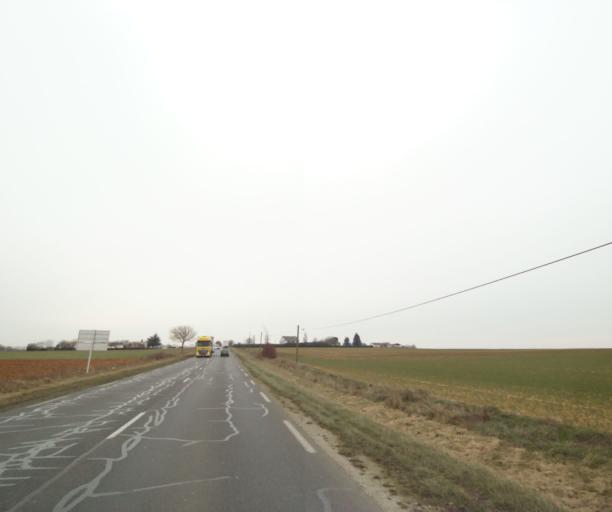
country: FR
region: Poitou-Charentes
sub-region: Departement des Deux-Sevres
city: Magne
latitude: 46.3515
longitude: -0.5198
